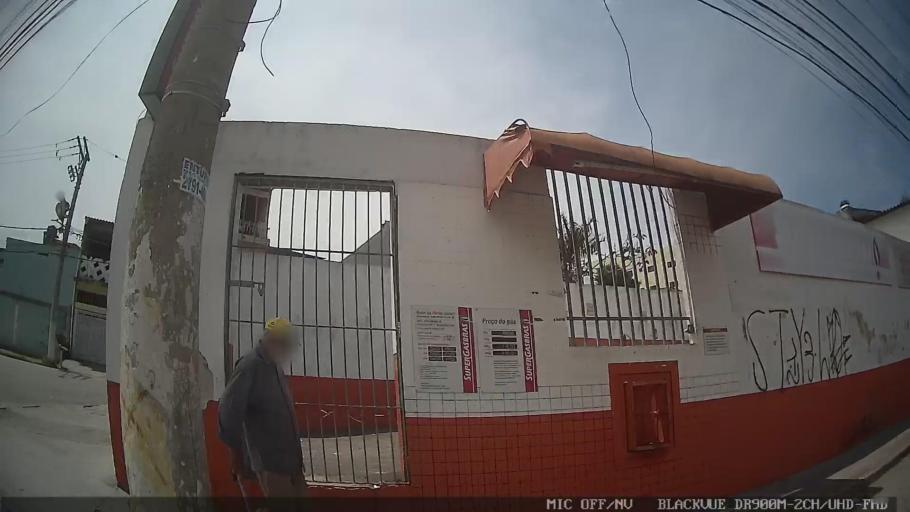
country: BR
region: Sao Paulo
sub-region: Ferraz De Vasconcelos
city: Ferraz de Vasconcelos
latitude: -23.5483
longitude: -46.3888
